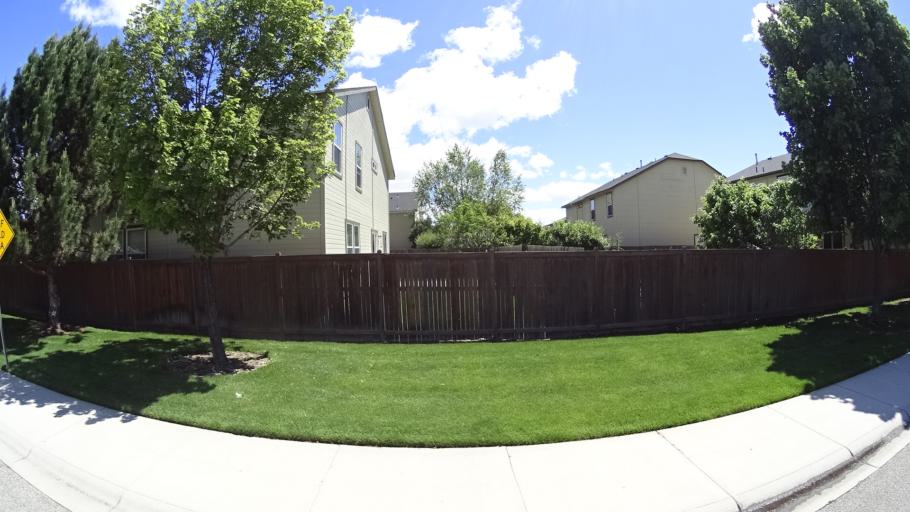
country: US
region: Idaho
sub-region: Ada County
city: Meridian
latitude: 43.6347
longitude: -116.3429
